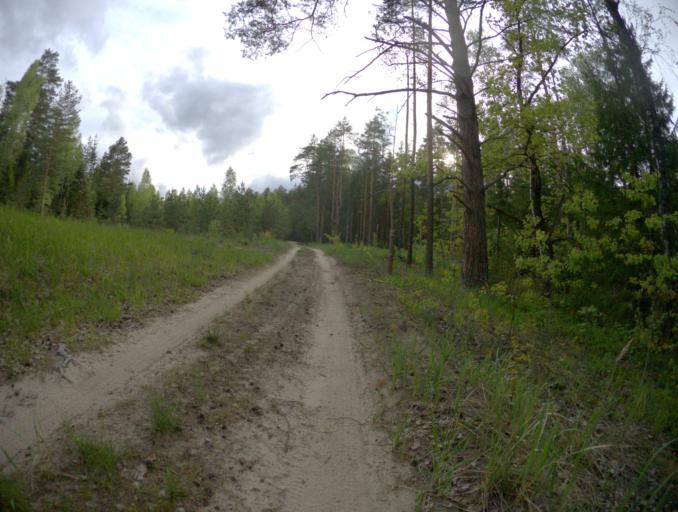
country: RU
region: Rjazan
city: Gus'-Zheleznyy
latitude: 55.1925
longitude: 41.0689
